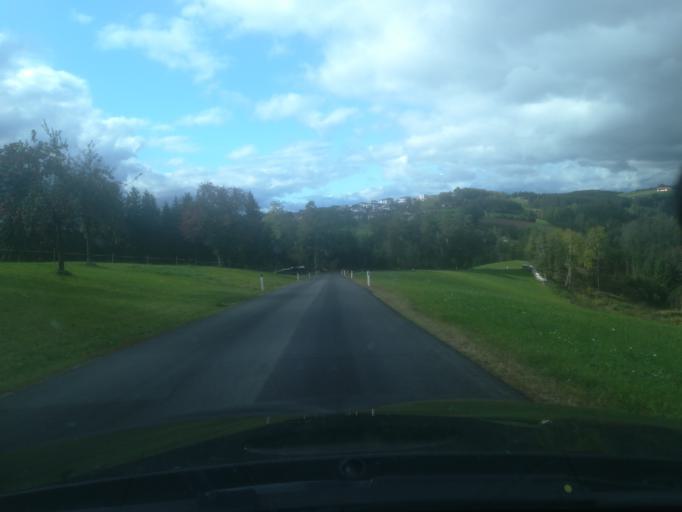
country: AT
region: Upper Austria
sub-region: Politischer Bezirk Urfahr-Umgebung
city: Herzogsdorf
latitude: 48.4251
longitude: 14.1418
